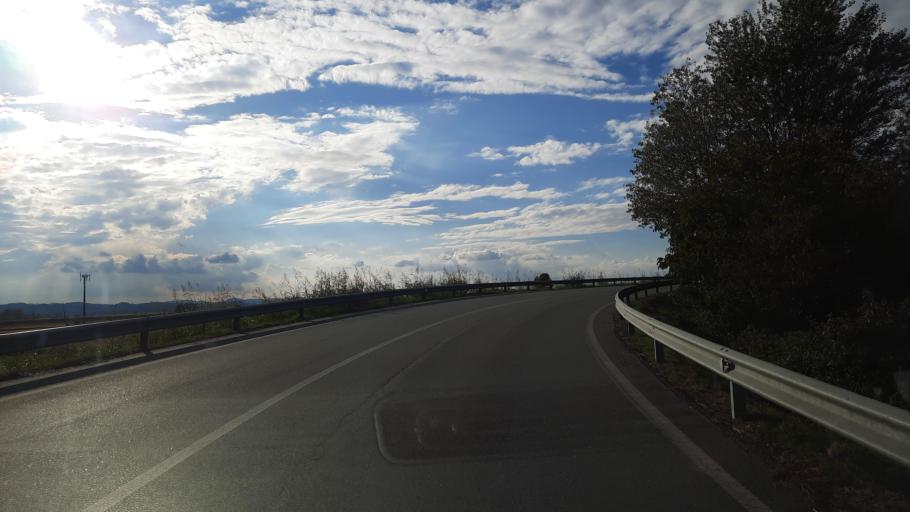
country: IT
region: Piedmont
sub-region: Provincia di Vercelli
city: Palazzolo Vercellese
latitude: 45.1879
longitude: 8.2249
